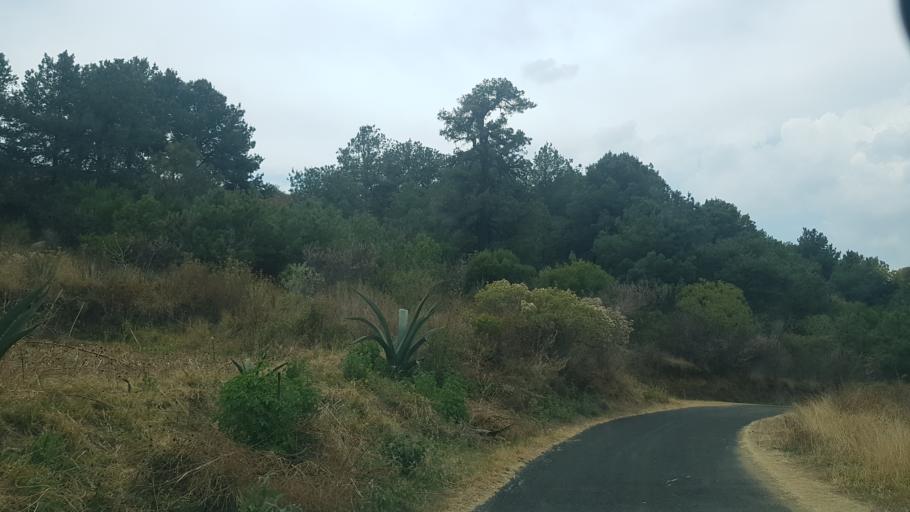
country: MX
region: Puebla
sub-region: Atzitzihuacan
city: Santiago Atzitzihuacan
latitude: 18.8402
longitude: -98.6119
